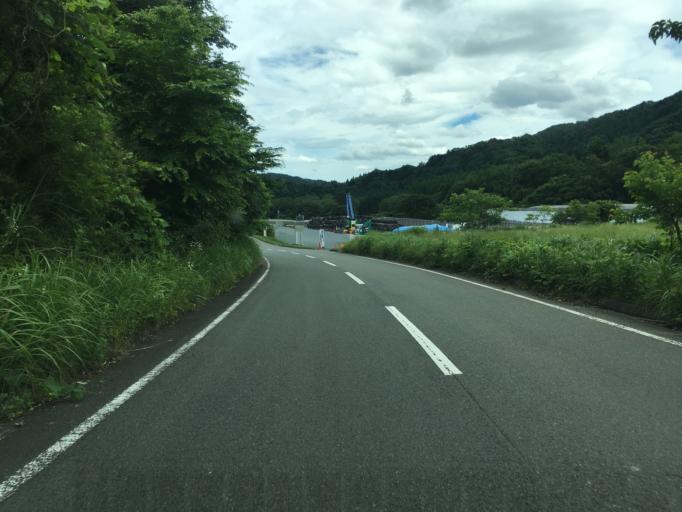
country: JP
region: Fukushima
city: Namie
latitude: 37.6964
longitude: 140.8800
